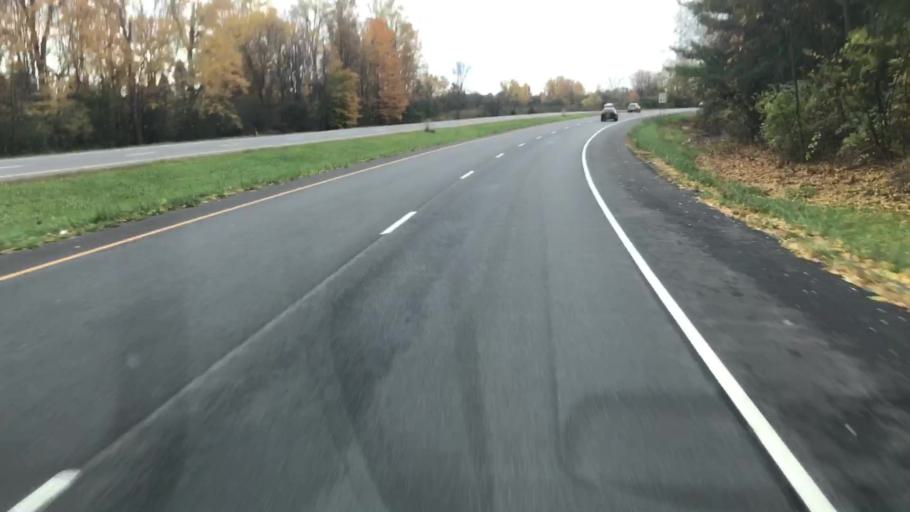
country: US
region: New York
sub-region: Onondaga County
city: Liverpool
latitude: 43.1346
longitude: -76.2092
